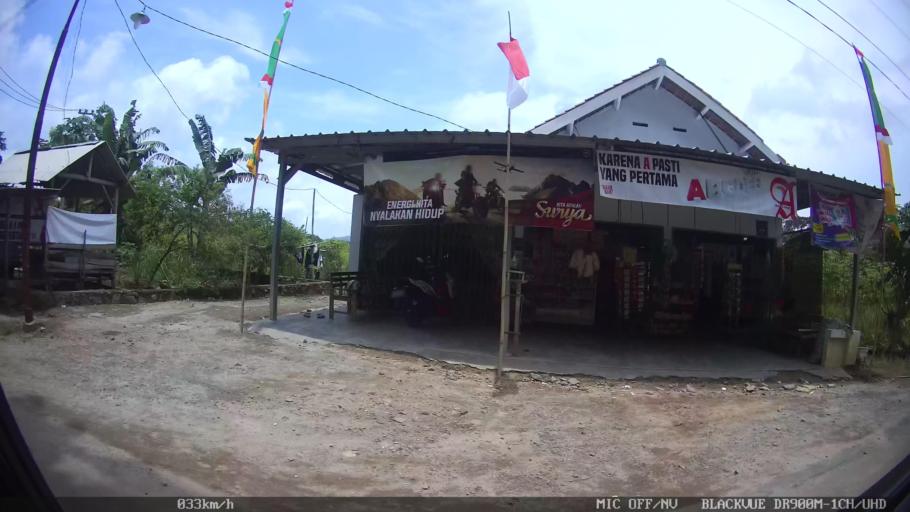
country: ID
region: Lampung
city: Bandarlampung
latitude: -5.4184
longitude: 105.2179
